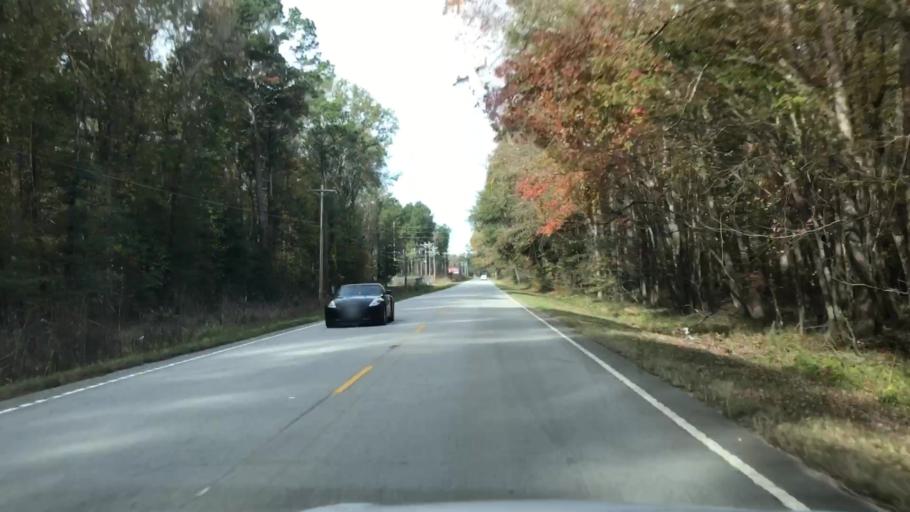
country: US
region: South Carolina
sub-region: Colleton County
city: Walterboro
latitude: 32.8201
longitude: -80.5495
